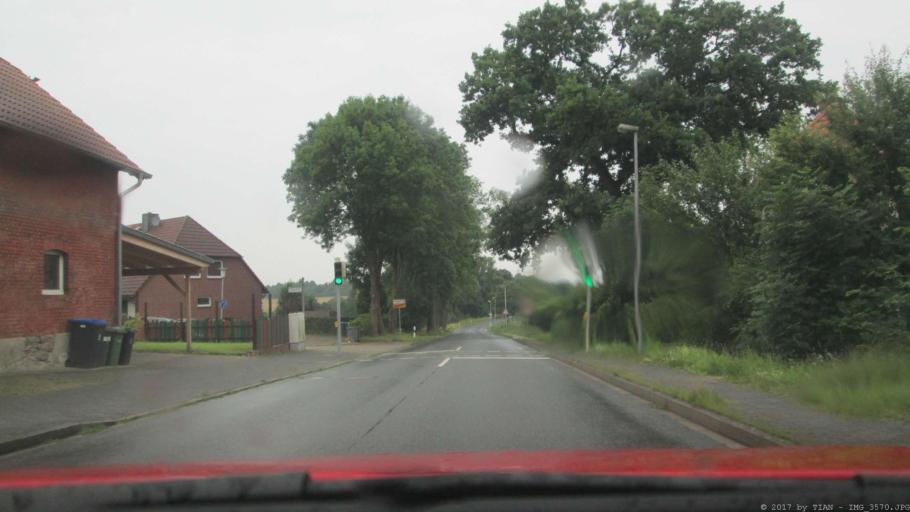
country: DE
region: Lower Saxony
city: Konigslutter am Elm
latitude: 52.3355
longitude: 10.8307
